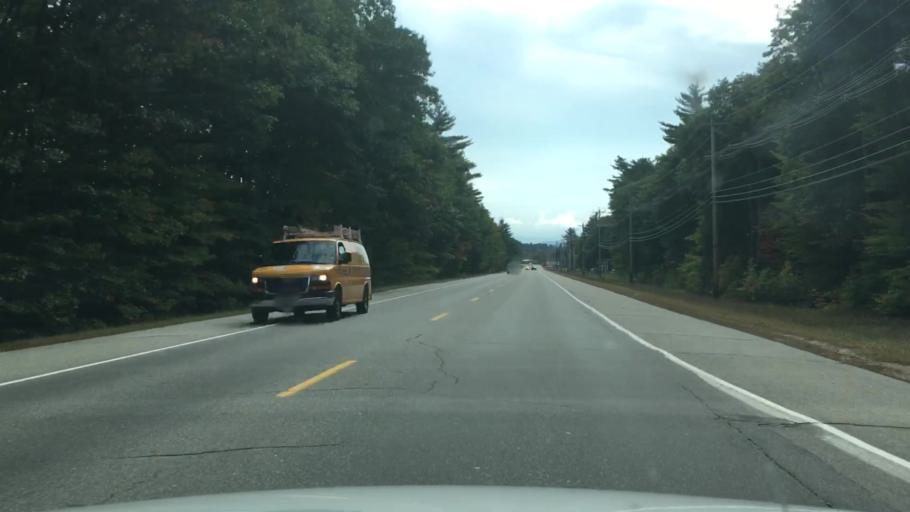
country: US
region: New Hampshire
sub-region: Carroll County
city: North Conway
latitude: 44.0960
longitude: -71.1506
